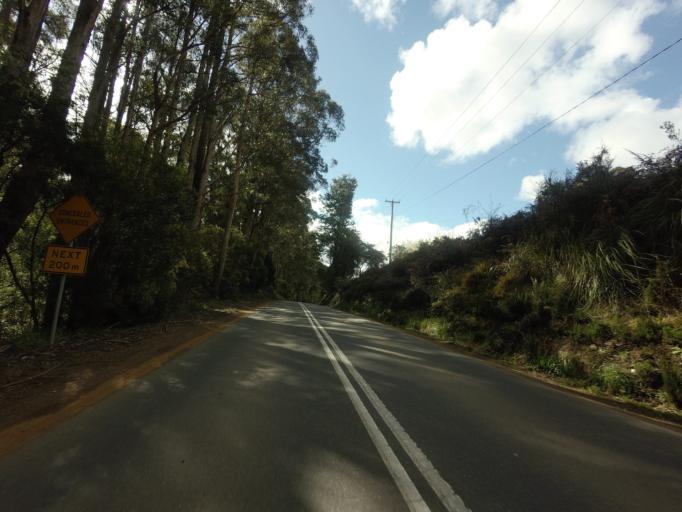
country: AU
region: Tasmania
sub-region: Huon Valley
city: Geeveston
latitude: -43.2230
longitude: 146.9879
